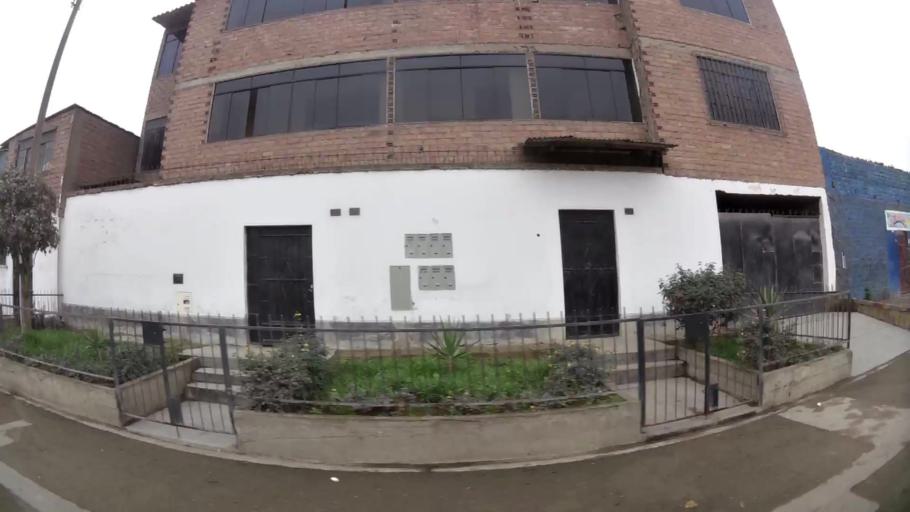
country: PE
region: Lima
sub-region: Lima
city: Surco
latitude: -12.1835
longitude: -76.9263
